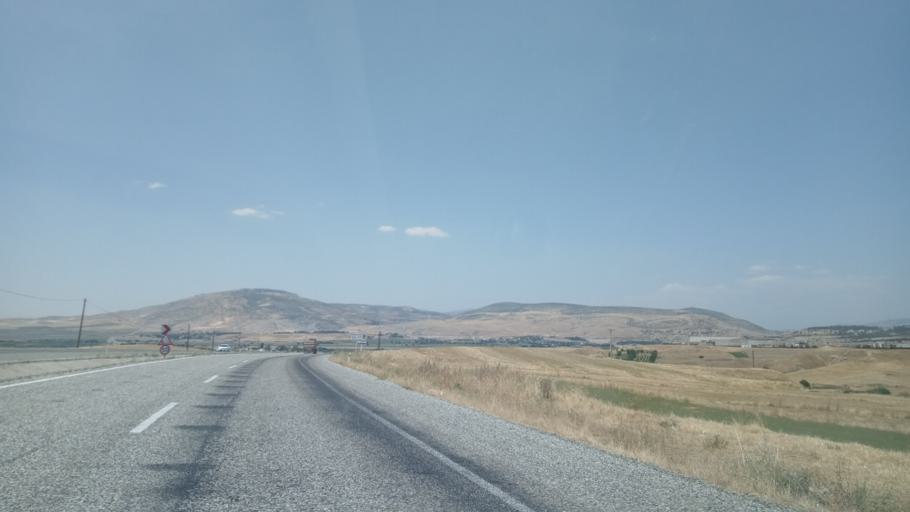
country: TR
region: Diyarbakir
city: Malabadi
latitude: 38.1339
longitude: 41.2432
